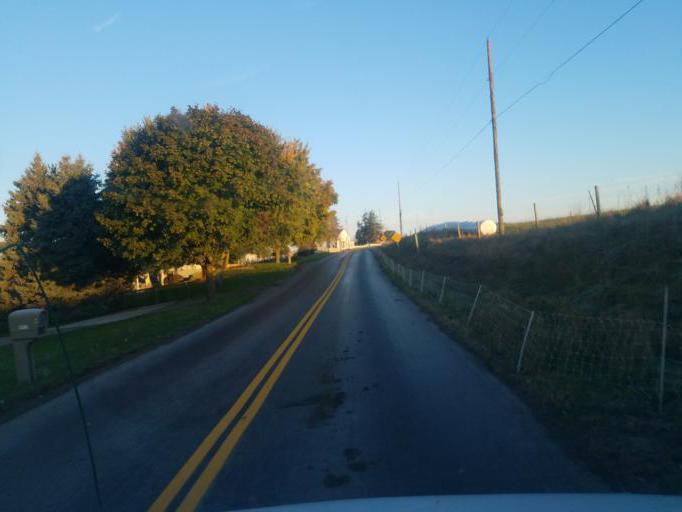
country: US
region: Ohio
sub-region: Stark County
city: Brewster
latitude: 40.6663
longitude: -81.7033
